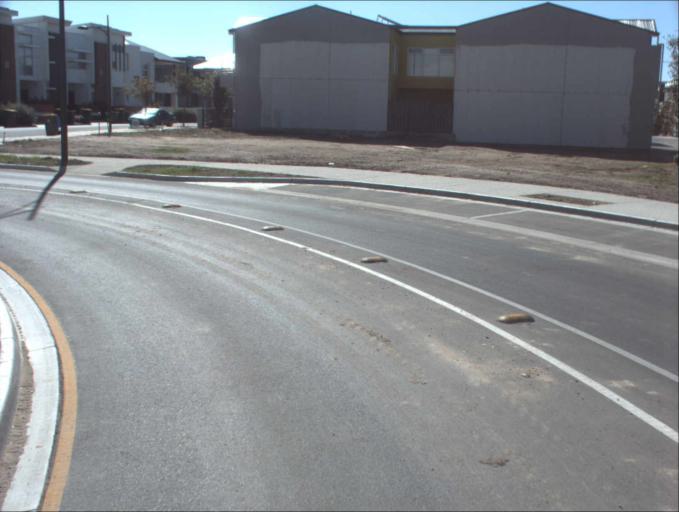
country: AU
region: South Australia
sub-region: Port Adelaide Enfield
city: Klemzig
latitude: -34.8633
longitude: 138.6304
